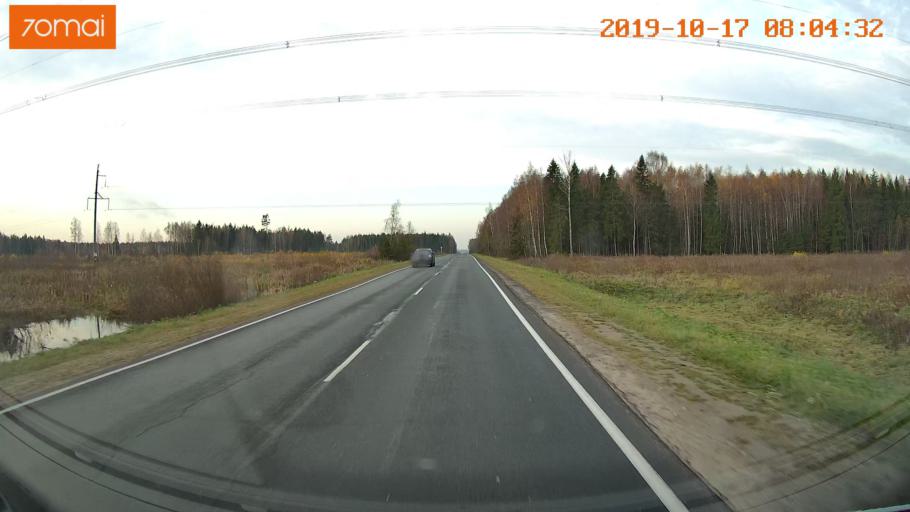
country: RU
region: Vladimir
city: Belaya Rechka
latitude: 56.3442
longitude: 39.4333
